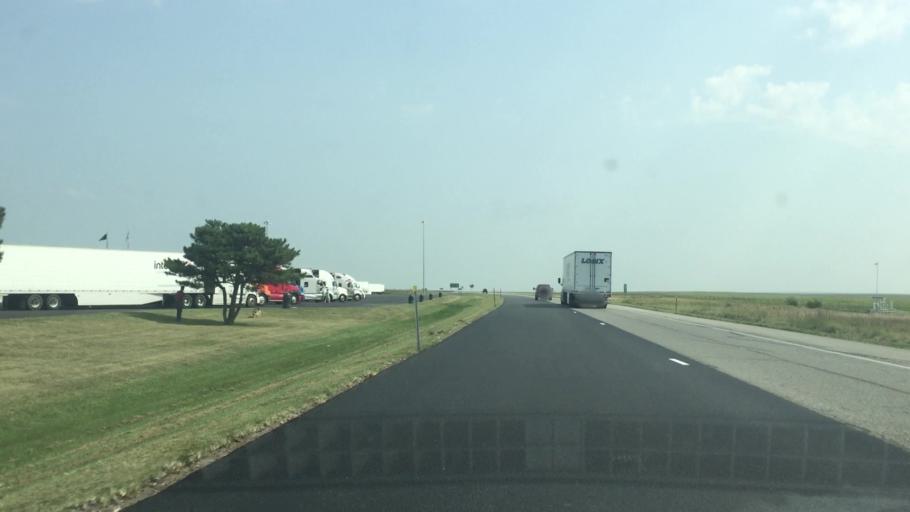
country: US
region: Kansas
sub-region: Chase County
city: Cottonwood Falls
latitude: 38.0942
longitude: -96.5793
